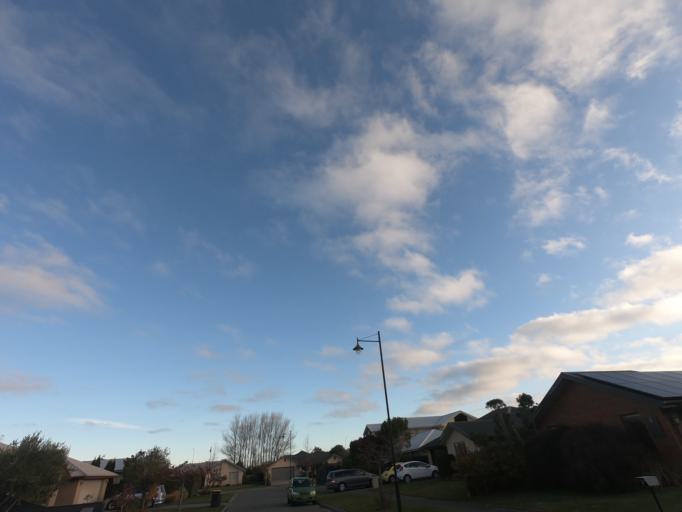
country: NZ
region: Canterbury
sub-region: Selwyn District
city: Prebbleton
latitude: -43.5680
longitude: 172.5646
